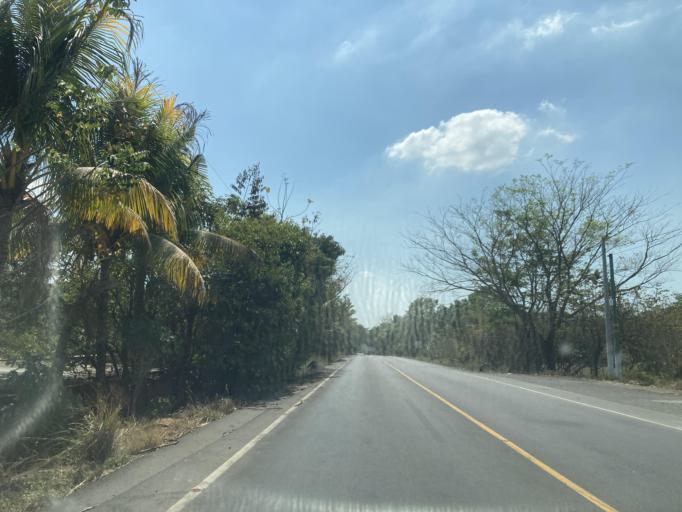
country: GT
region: Escuintla
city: Guanagazapa
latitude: 14.2049
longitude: -90.7149
